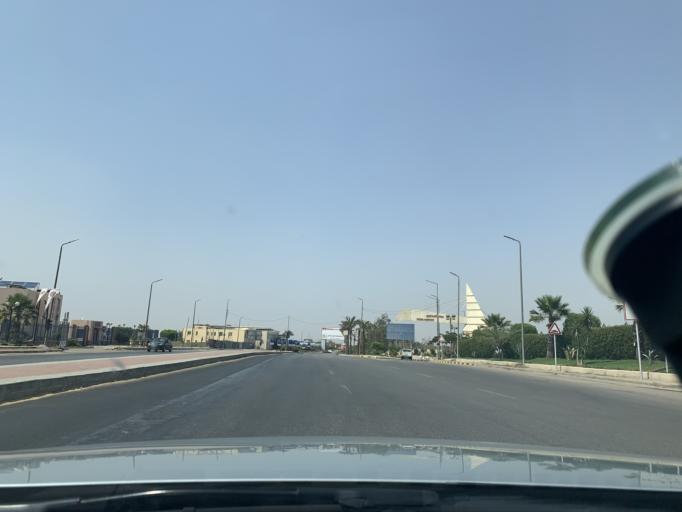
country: EG
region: Muhafazat al Qalyubiyah
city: Al Khankah
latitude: 30.0941
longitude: 31.3827
